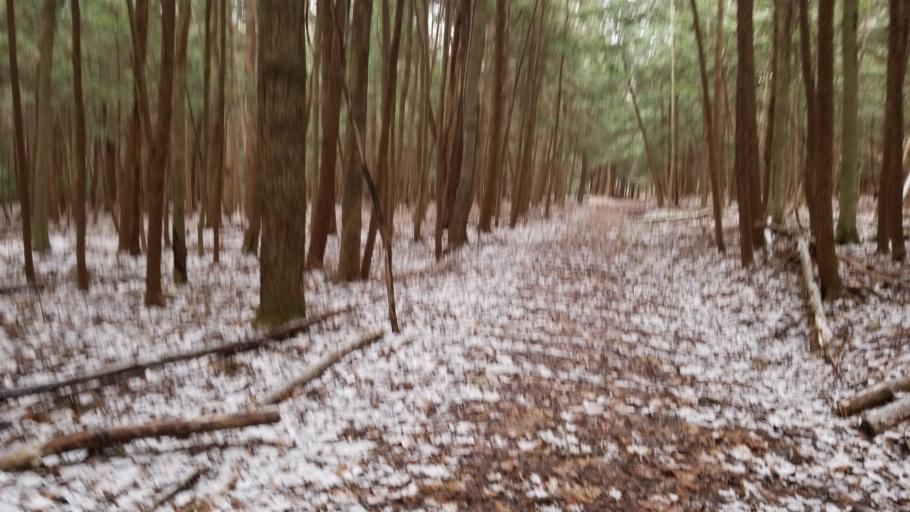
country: US
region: Pennsylvania
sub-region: Clearfield County
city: Clearfield
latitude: 41.1864
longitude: -78.5283
